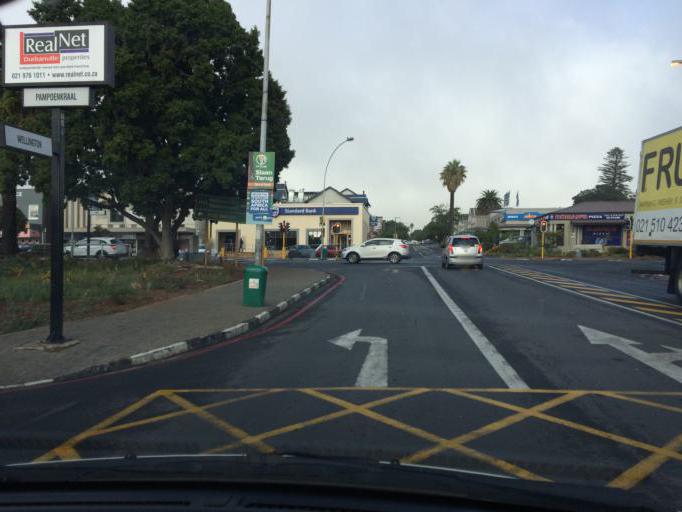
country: ZA
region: Western Cape
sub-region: City of Cape Town
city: Kraaifontein
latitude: -33.8321
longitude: 18.6471
